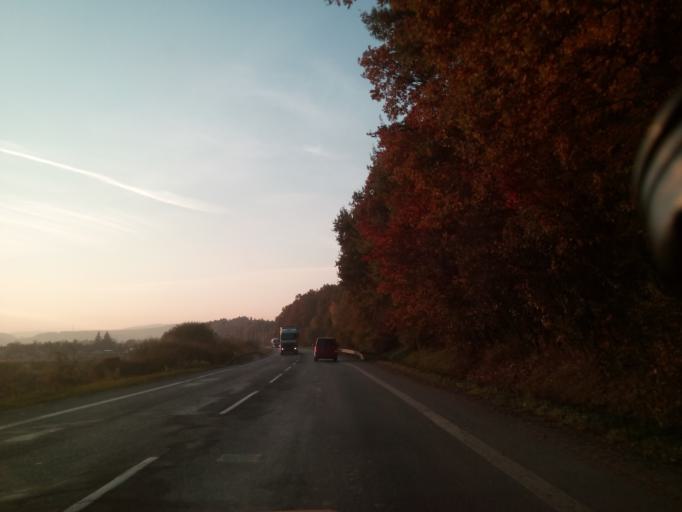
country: SK
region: Presovsky
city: Sabinov
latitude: 49.0042
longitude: 21.0977
